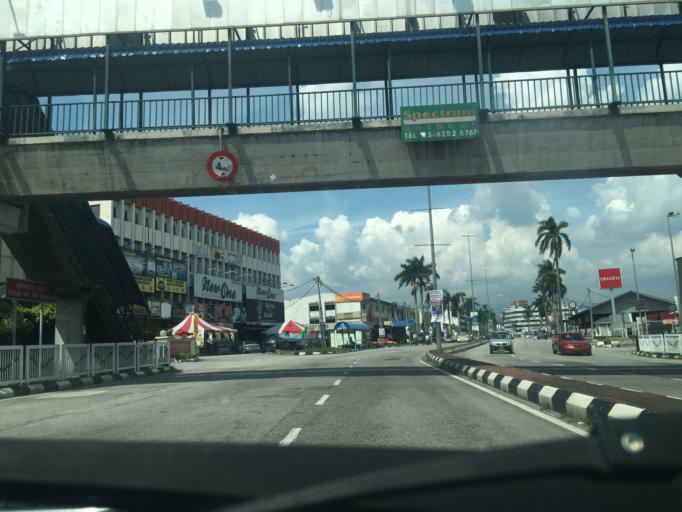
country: MY
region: Perak
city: Ipoh
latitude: 4.5844
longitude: 101.0908
